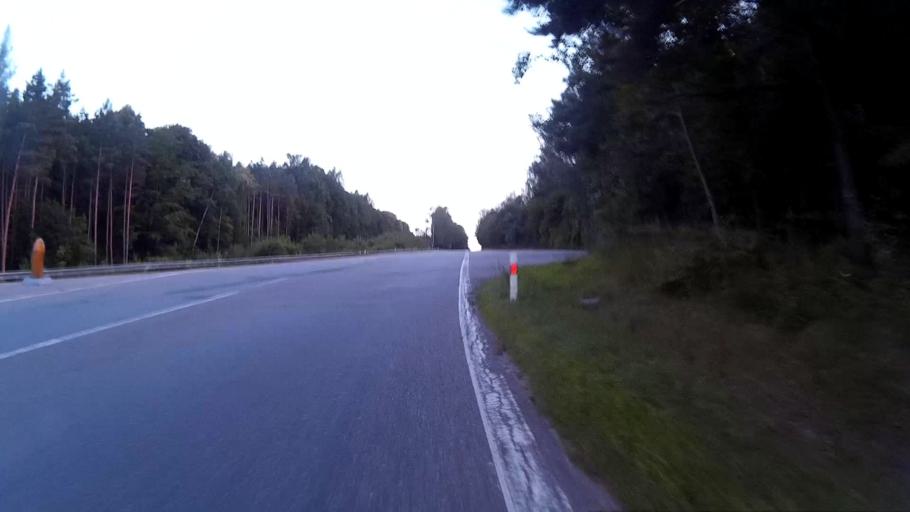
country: CZ
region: South Moravian
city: Troubsko
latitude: 49.1987
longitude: 16.5146
